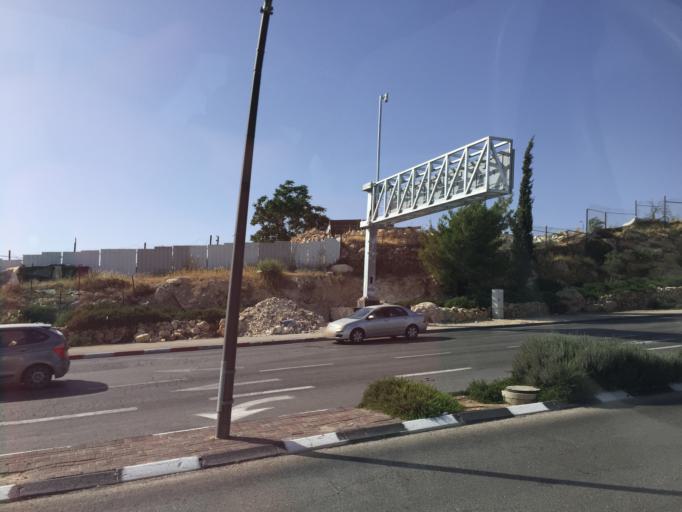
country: PS
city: Khallat Hamamah
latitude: 31.7320
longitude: 35.2067
